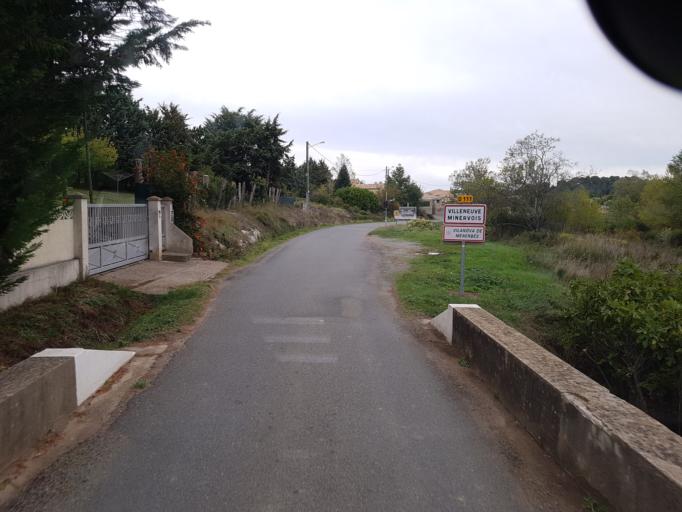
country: FR
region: Languedoc-Roussillon
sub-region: Departement de l'Aude
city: Conques-sur-Orbiel
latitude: 43.3150
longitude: 2.4551
